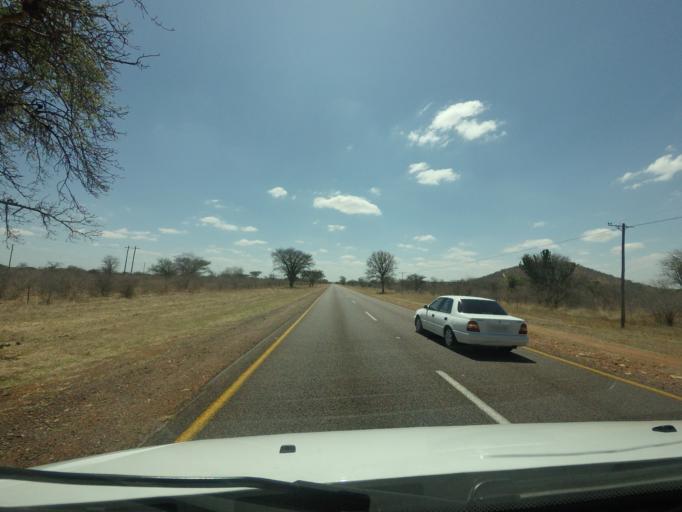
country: ZA
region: Limpopo
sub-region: Capricorn District Municipality
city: Dendron
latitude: -23.6213
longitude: 28.8267
